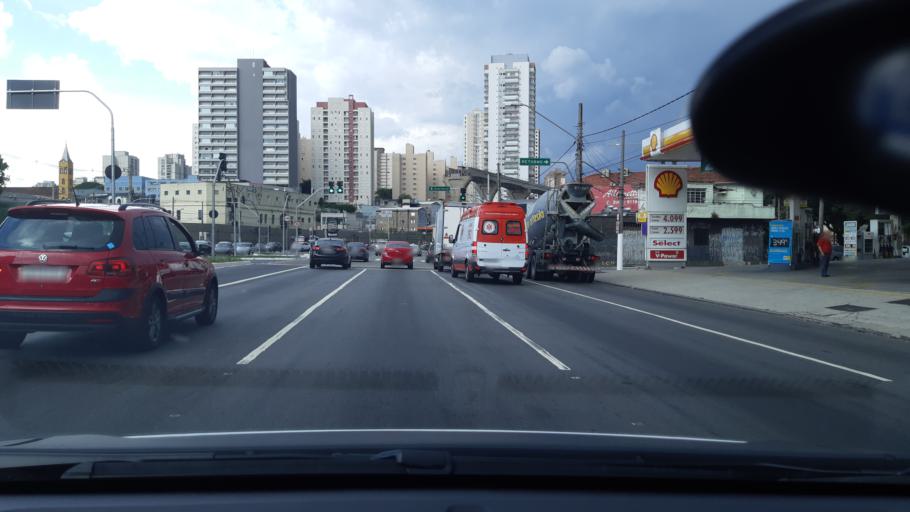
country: BR
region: Sao Paulo
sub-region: Sao Caetano Do Sul
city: Sao Caetano do Sul
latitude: -23.5847
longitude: -46.5867
